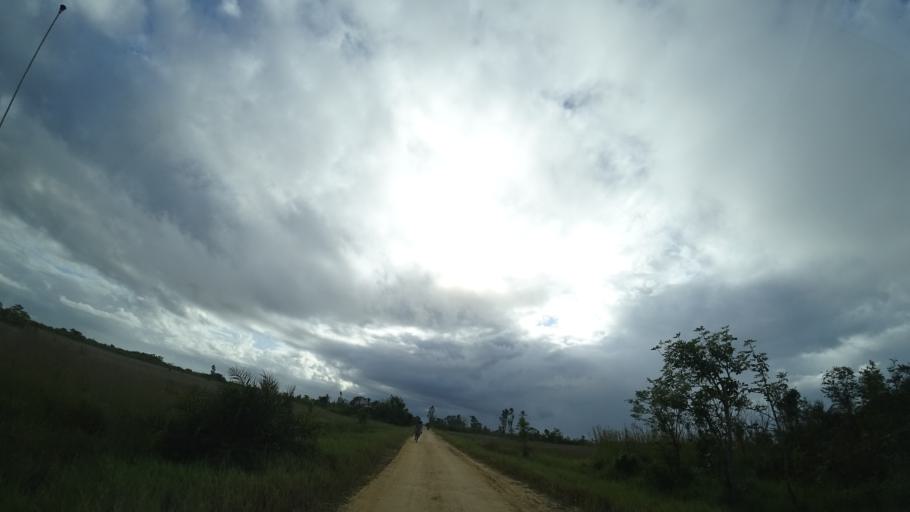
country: MZ
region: Sofala
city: Beira
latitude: -19.6928
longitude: 35.0384
